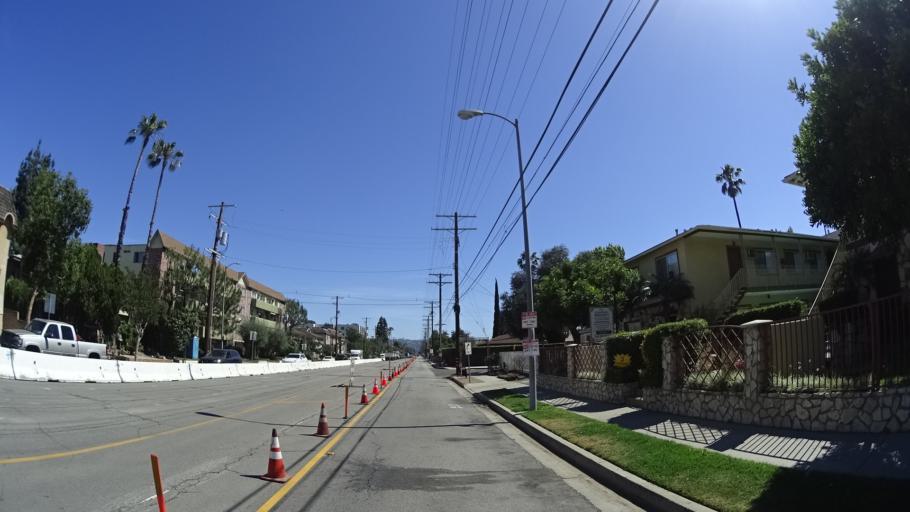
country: US
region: California
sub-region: Los Angeles County
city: North Hollywood
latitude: 34.1781
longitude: -118.4054
